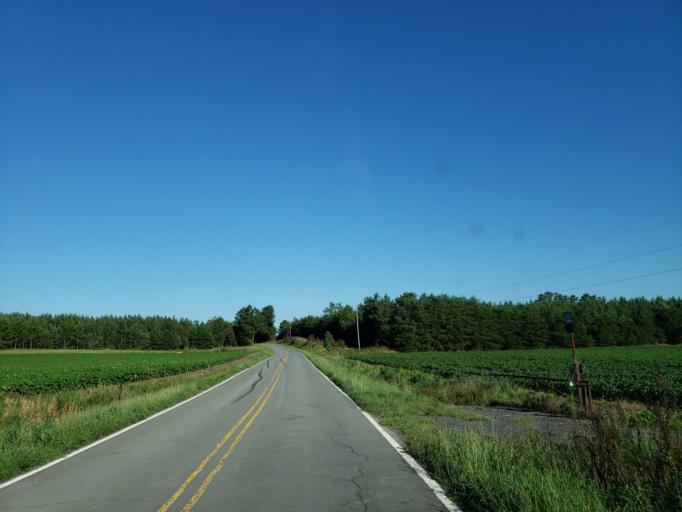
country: US
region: Georgia
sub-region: Polk County
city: Aragon
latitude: 34.1058
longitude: -85.0177
